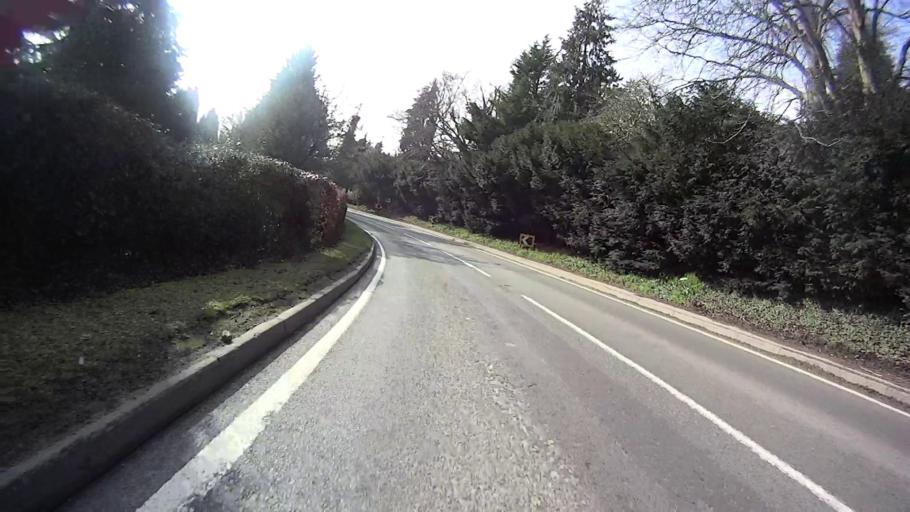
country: GB
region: England
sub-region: Surrey
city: Headley
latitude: 51.2532
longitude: -0.2654
